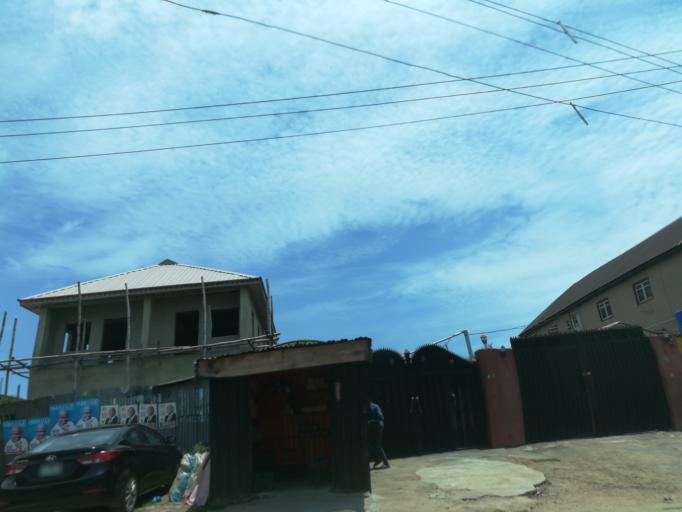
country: NG
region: Lagos
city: Ebute Ikorodu
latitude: 6.6030
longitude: 3.4889
